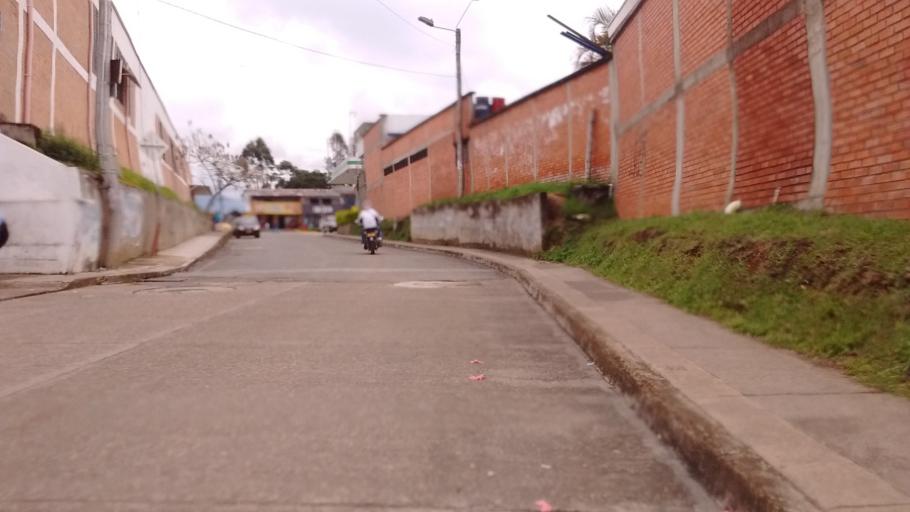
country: CO
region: Cauca
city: Popayan
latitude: 2.4802
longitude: -76.5762
